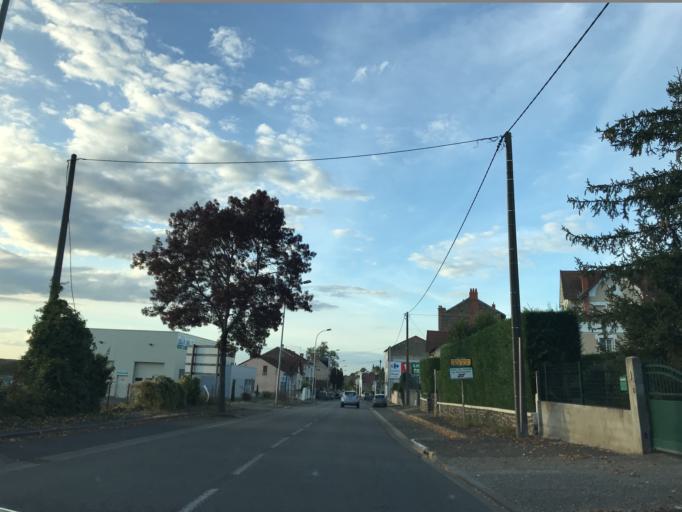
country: FR
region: Auvergne
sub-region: Departement de l'Allier
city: Abrest
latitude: 46.1126
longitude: 3.4408
